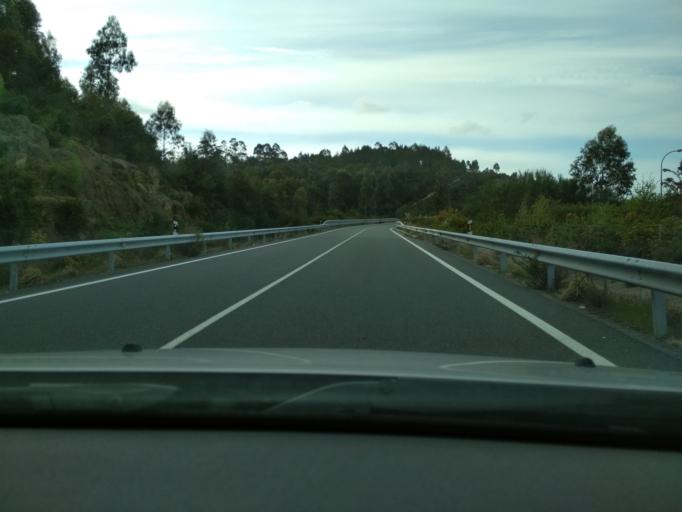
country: ES
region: Galicia
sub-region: Provincia da Coruna
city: Culleredo
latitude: 43.2875
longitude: -8.4004
